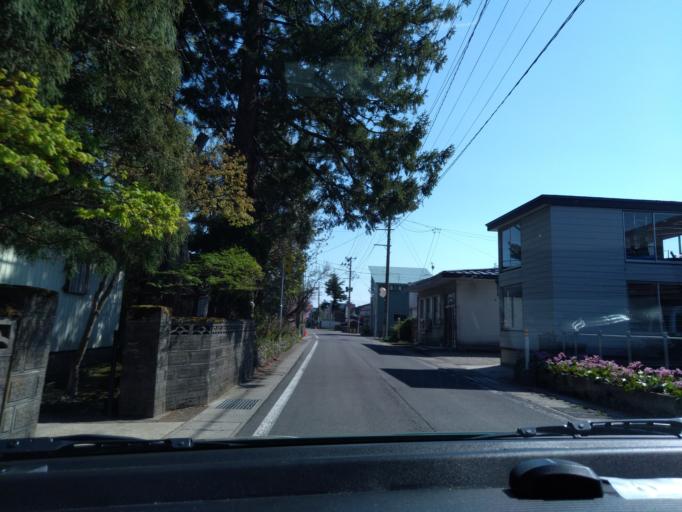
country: JP
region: Akita
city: Kakunodatemachi
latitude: 39.5029
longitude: 140.5948
